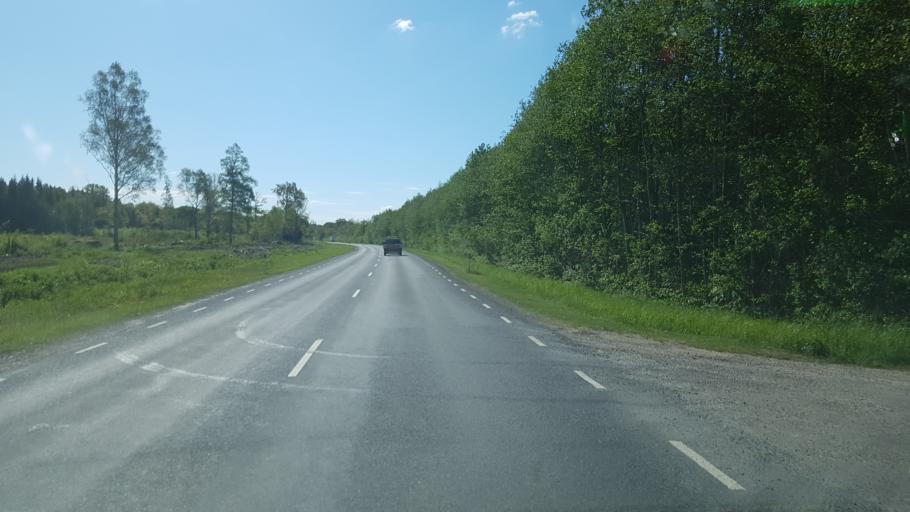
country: EE
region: Laeaene
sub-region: Ridala Parish
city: Uuemoisa
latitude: 58.8411
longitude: 23.6516
